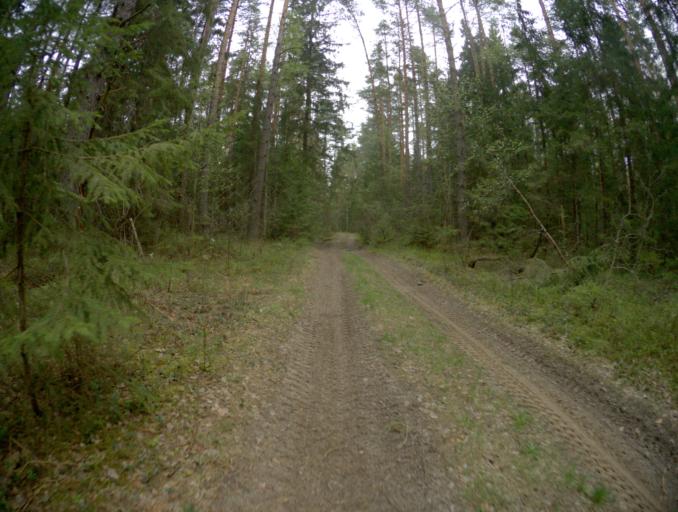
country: RU
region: Vladimir
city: Golovino
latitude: 55.8964
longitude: 40.4388
